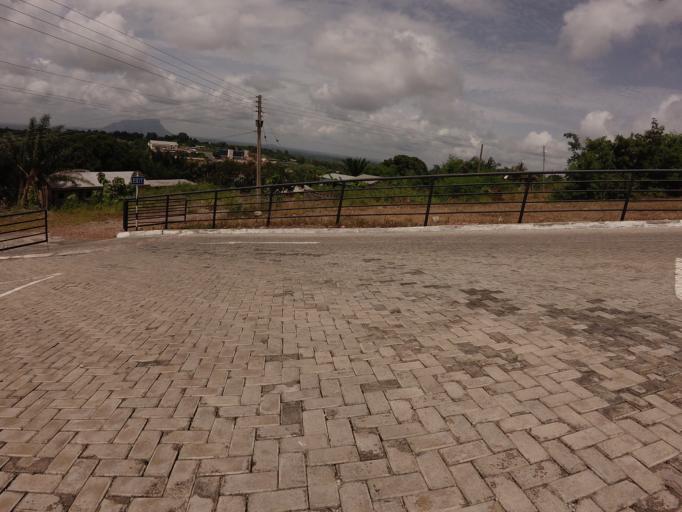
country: GH
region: Volta
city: Ho
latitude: 6.6141
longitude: 0.4549
